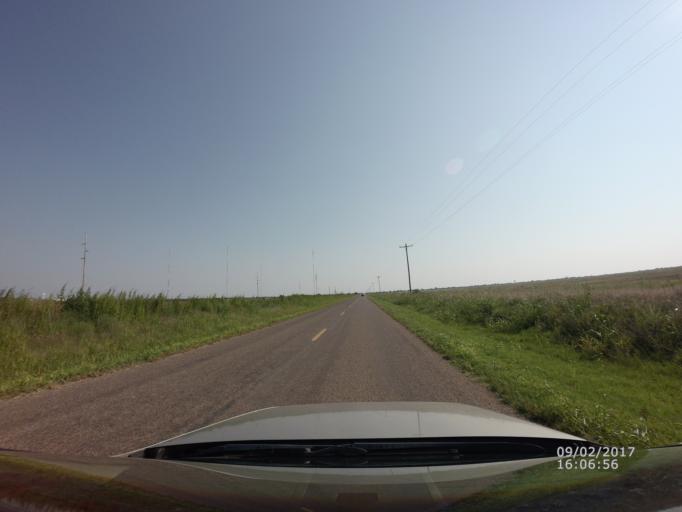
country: US
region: New Mexico
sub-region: Curry County
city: Clovis
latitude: 34.4456
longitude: -103.2140
